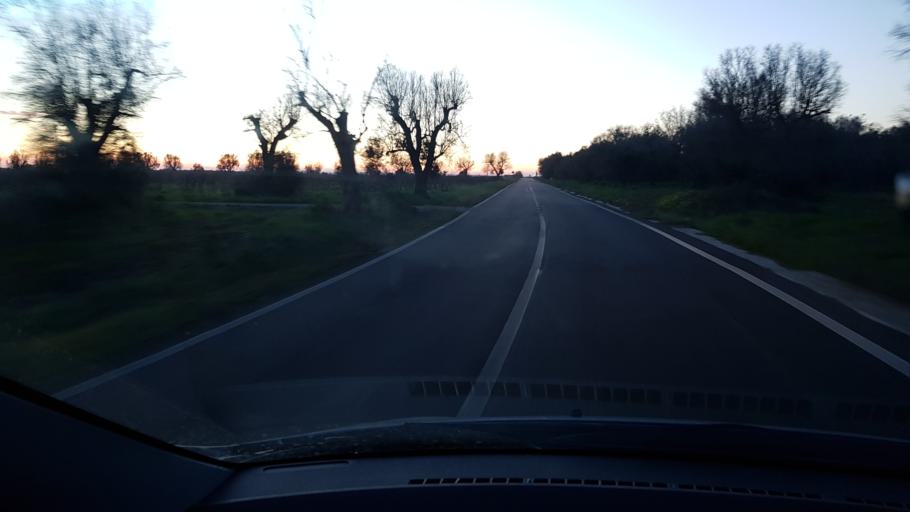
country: IT
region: Apulia
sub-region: Provincia di Brindisi
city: Tuturano
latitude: 40.5272
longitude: 17.9104
